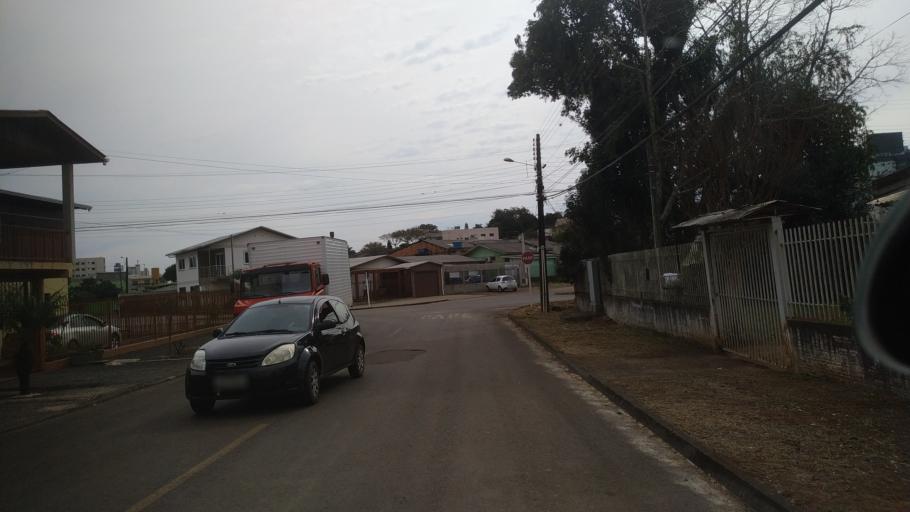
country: BR
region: Santa Catarina
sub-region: Chapeco
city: Chapeco
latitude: -27.1147
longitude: -52.6000
